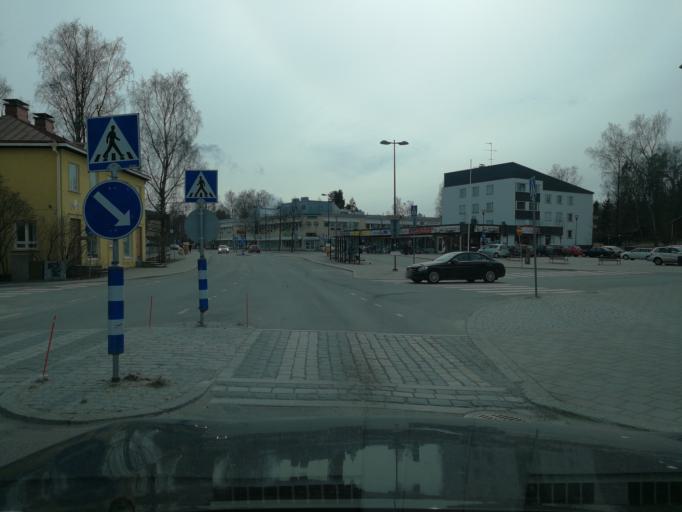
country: FI
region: Uusimaa
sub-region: Helsinki
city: Lohja
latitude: 60.1916
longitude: 23.9993
